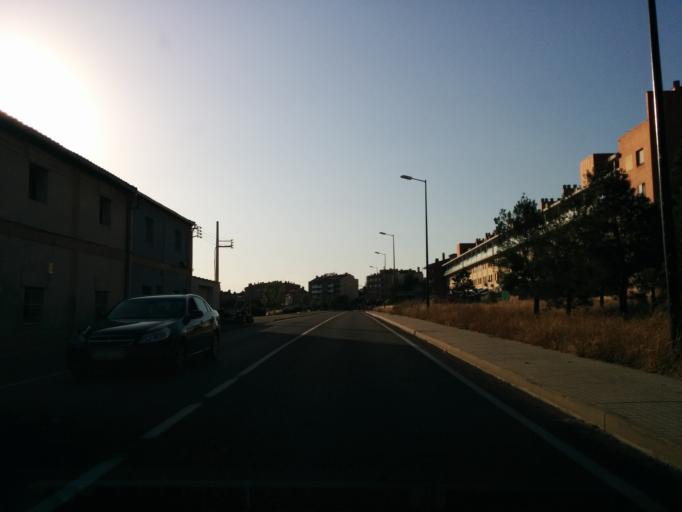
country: ES
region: Aragon
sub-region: Provincia de Zaragoza
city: Zaragoza
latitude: 41.6646
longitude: -0.8230
